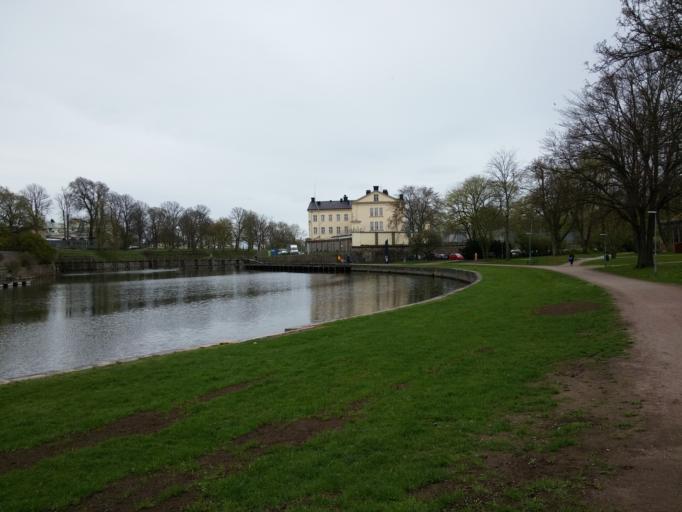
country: SE
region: Kalmar
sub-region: Kalmar Kommun
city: Kalmar
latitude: 56.6650
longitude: 16.3578
